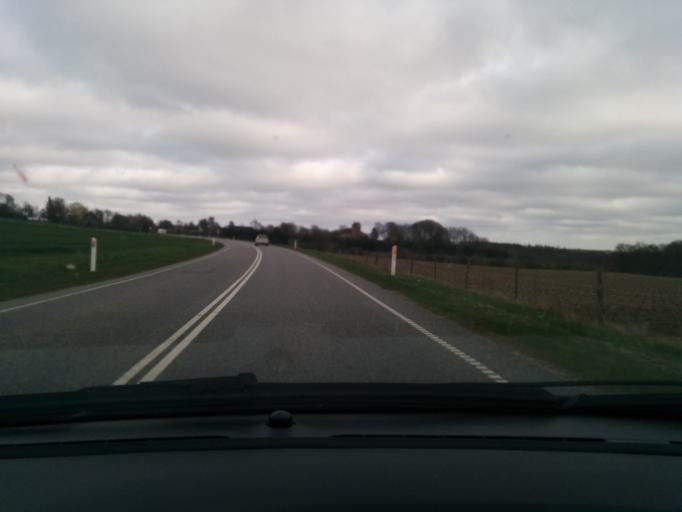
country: DK
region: Central Jutland
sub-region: Favrskov Kommune
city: Hammel
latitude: 56.2102
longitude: 9.8012
